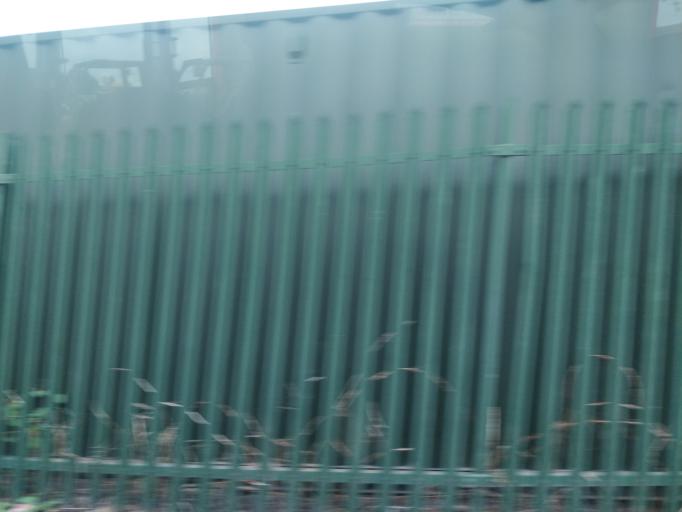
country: GB
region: England
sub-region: Lancashire
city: Ormskirk
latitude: 53.5984
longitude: -2.8656
